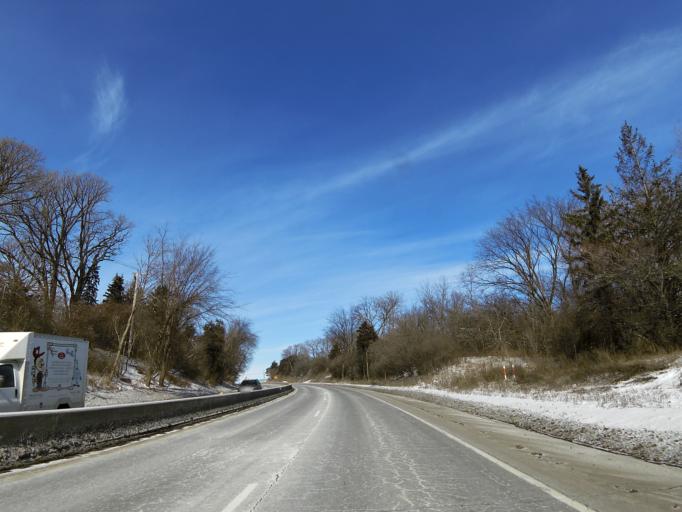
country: US
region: Minnesota
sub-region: Dakota County
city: Hastings
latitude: 44.7618
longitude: -92.8540
